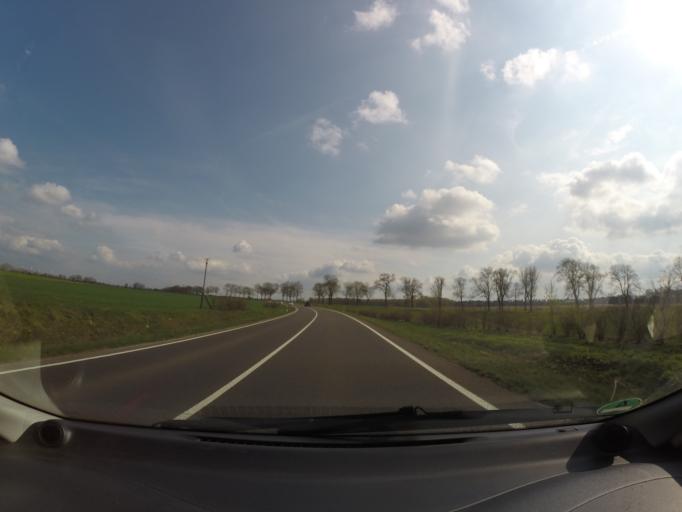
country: DE
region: Brandenburg
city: Rehfelde
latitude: 52.4822
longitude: 13.8819
